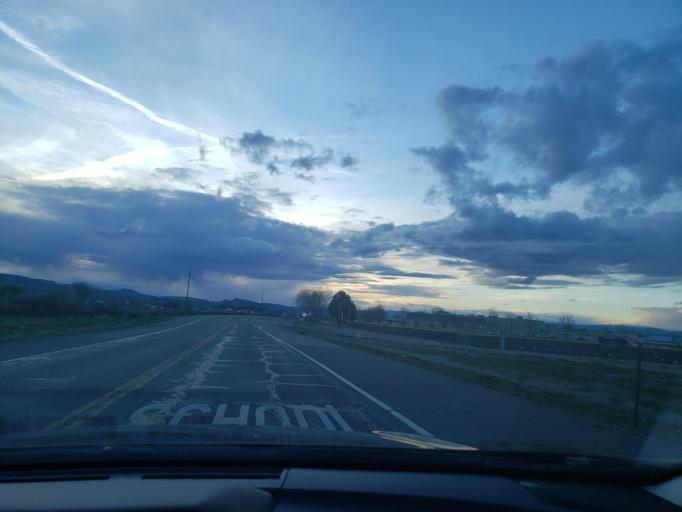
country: US
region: Colorado
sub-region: Mesa County
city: Fruita
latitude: 39.1458
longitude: -108.7136
